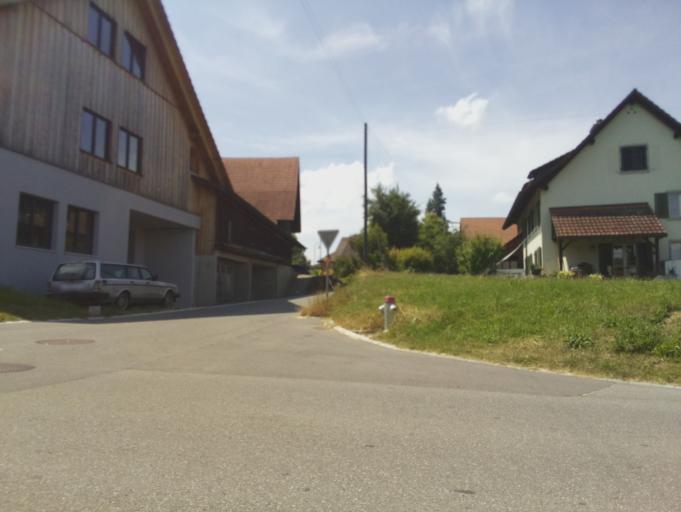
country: CH
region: Zurich
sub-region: Bezirk Andelfingen
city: Marthalen
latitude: 47.6231
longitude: 8.6495
